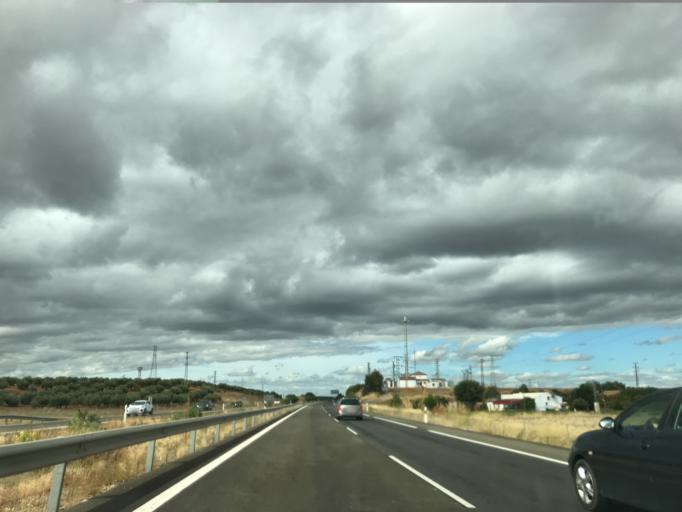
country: ES
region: Andalusia
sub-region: Province of Cordoba
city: Villa del Rio
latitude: 37.9874
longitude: -4.3089
